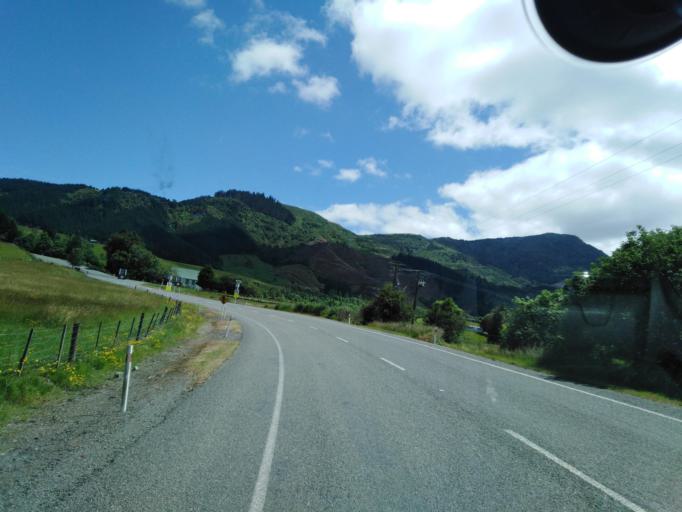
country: NZ
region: Nelson
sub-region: Nelson City
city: Nelson
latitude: -41.2124
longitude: 173.3958
